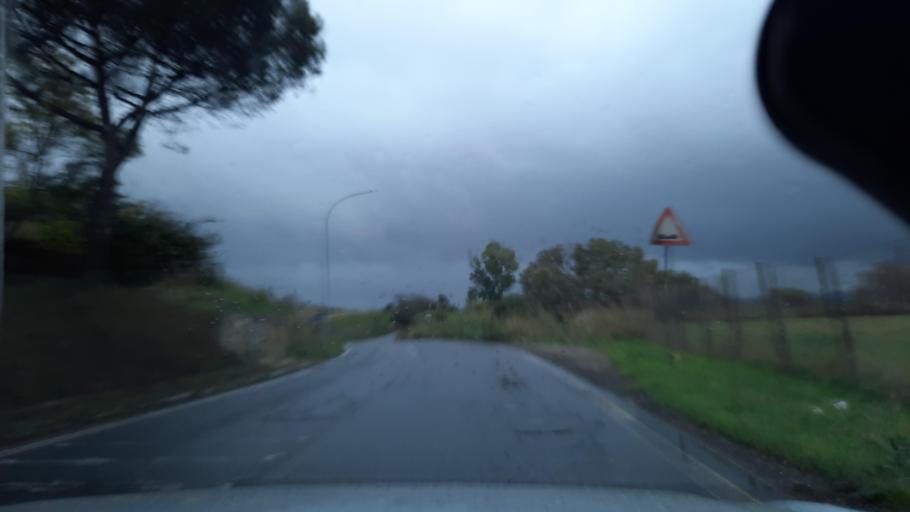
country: IT
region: Latium
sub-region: Citta metropolitana di Roma Capitale
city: Ponte Galeria-La Pisana
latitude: 41.8188
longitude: 12.3555
